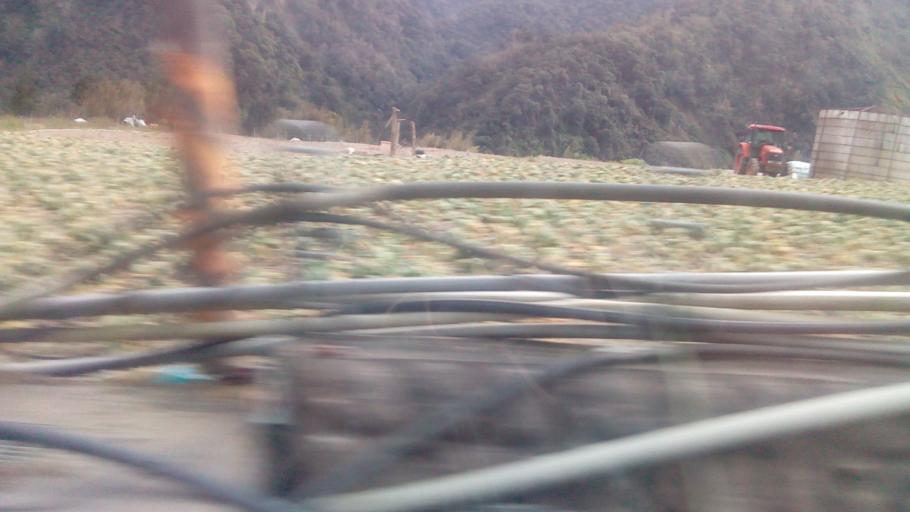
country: TW
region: Taiwan
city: Daxi
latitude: 24.4696
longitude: 121.4077
